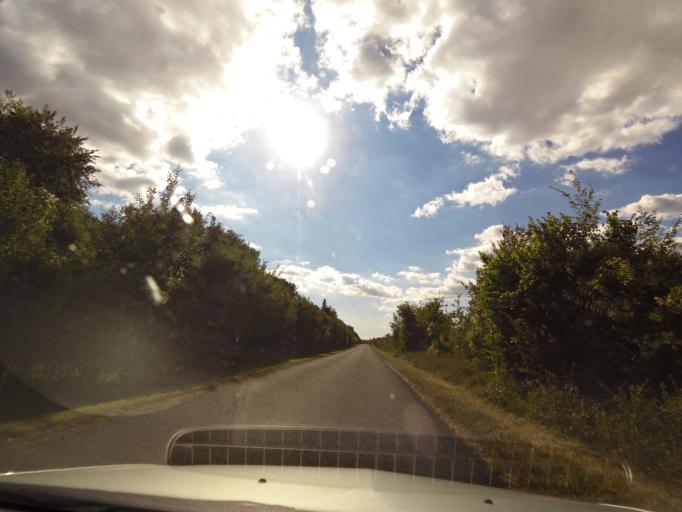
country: FR
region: Poitou-Charentes
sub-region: Departement des Deux-Sevres
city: Beauvoir-sur-Niort
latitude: 46.1480
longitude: -0.4366
